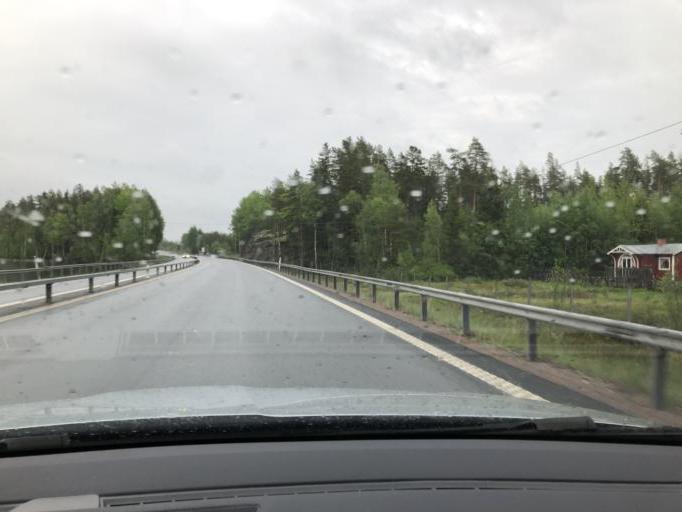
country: SE
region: Vaesterbotten
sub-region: Umea Kommun
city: Hoernefors
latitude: 63.6146
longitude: 19.8179
